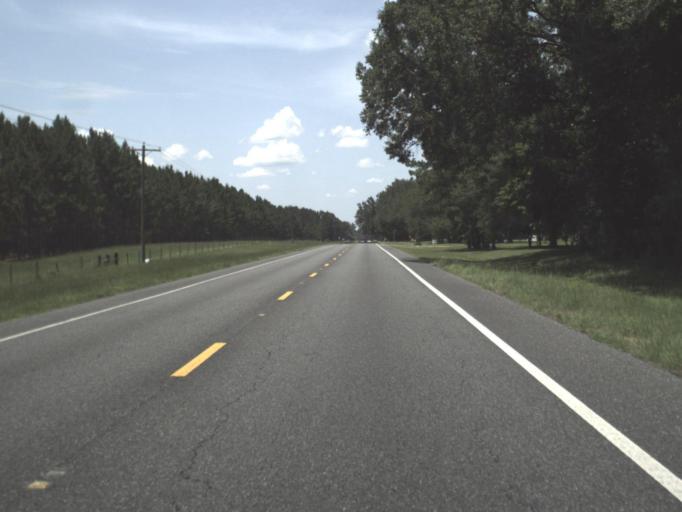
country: US
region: Florida
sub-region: Gilchrist County
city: Trenton
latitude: 29.5799
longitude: -82.8232
